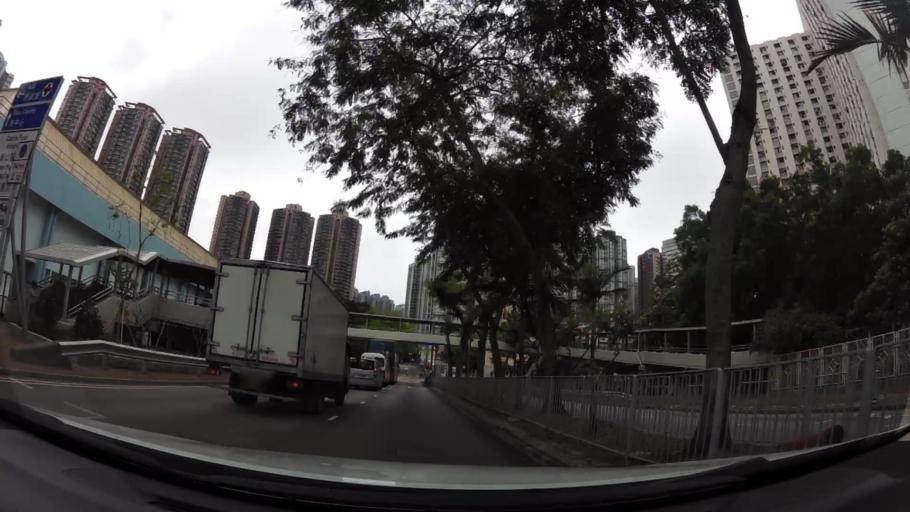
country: HK
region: Tuen Mun
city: Tuen Mun
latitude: 22.4037
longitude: 113.9728
